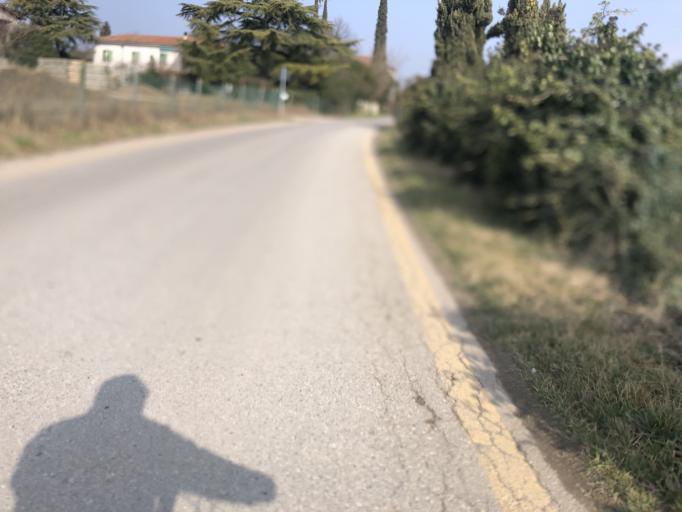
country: IT
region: Veneto
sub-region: Provincia di Verona
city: San Giorgio in Salici
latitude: 45.4225
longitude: 10.7970
